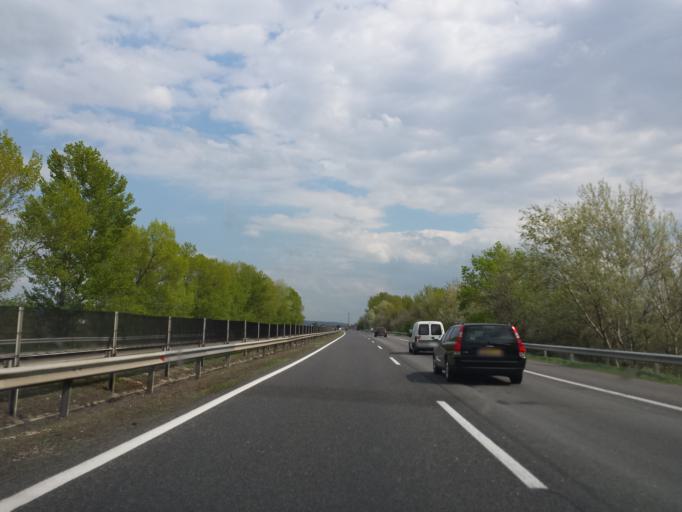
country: HU
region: Komarom-Esztergom
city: Kocs
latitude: 47.6291
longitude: 18.2594
